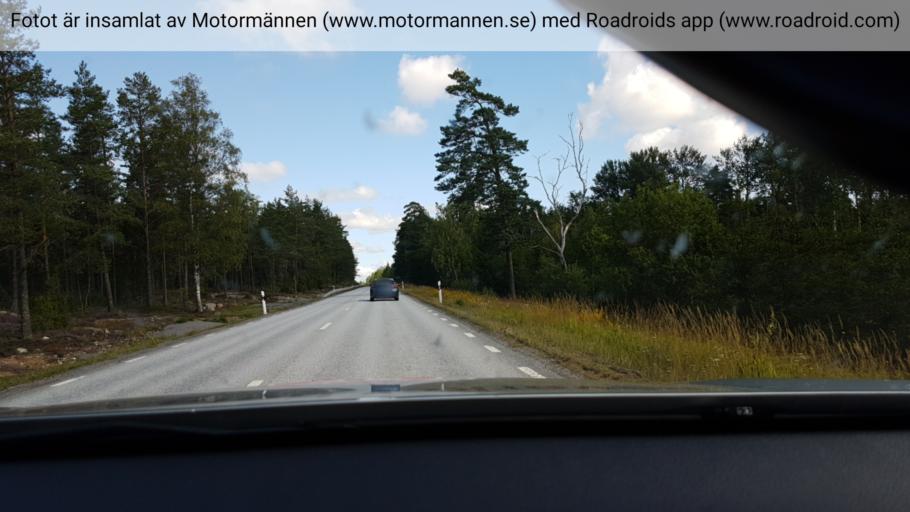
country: SE
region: Stockholm
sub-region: Norrtalje Kommun
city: Norrtalje
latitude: 59.6985
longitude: 18.6637
